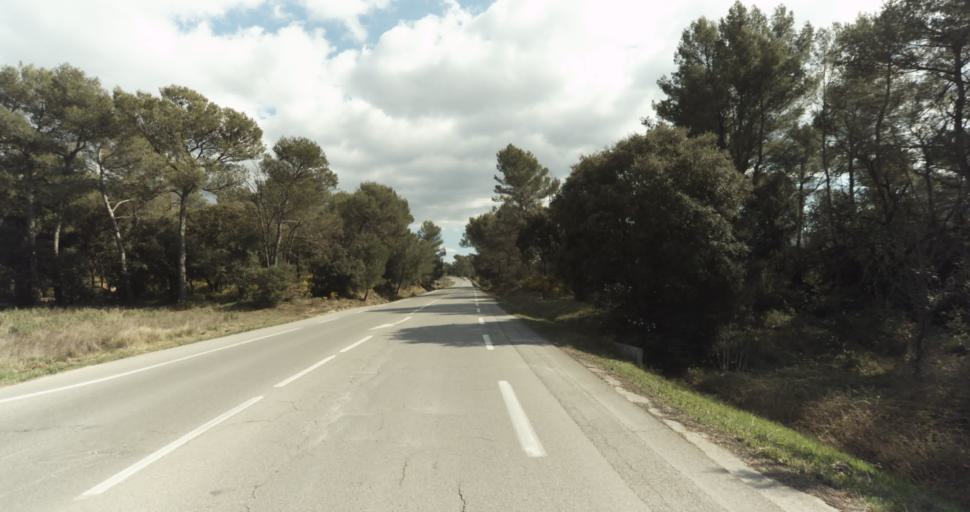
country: FR
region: Provence-Alpes-Cote d'Azur
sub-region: Departement des Bouches-du-Rhone
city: Greasque
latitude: 43.4457
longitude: 5.5236
